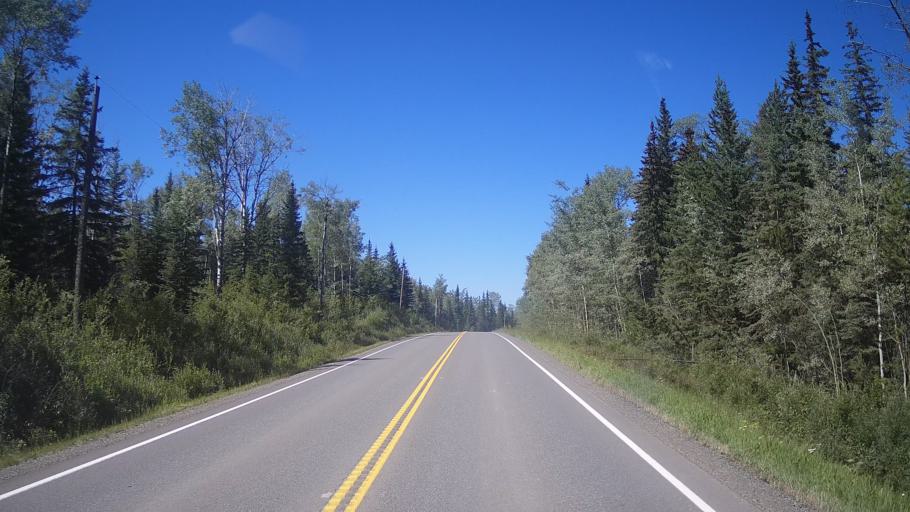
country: CA
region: British Columbia
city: Cache Creek
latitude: 51.5466
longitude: -120.9305
